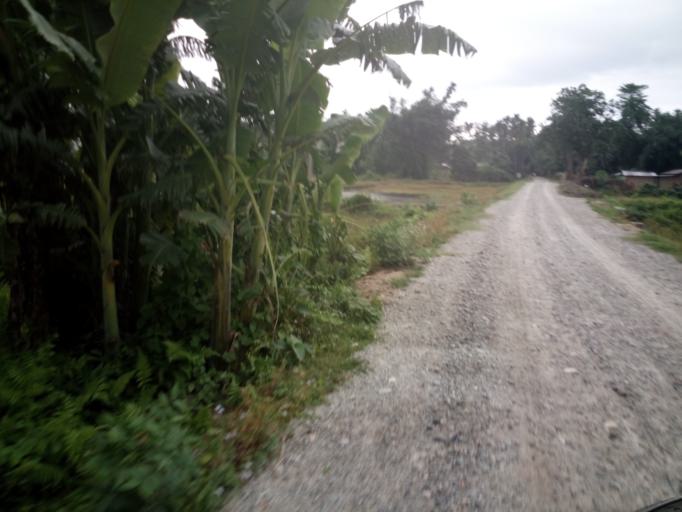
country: IN
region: Assam
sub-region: Darrang
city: Kharupatia
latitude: 26.6512
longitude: 92.2405
